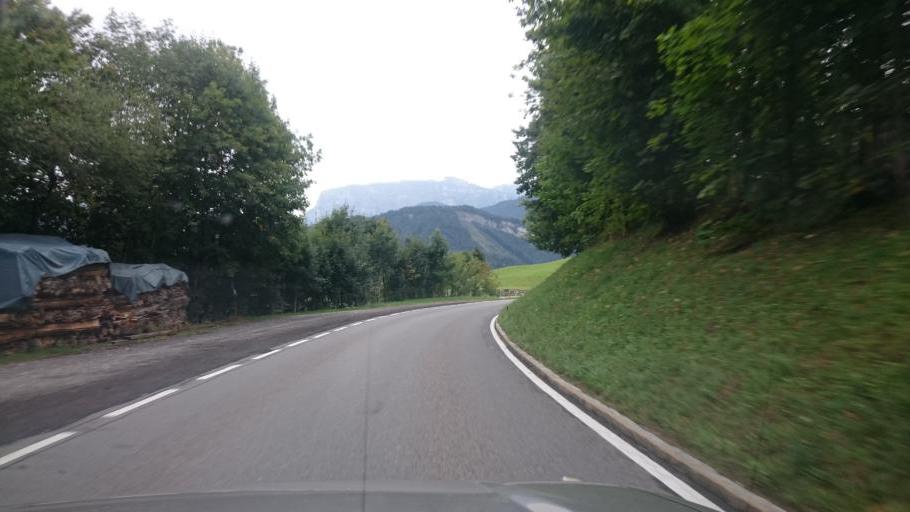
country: AT
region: Vorarlberg
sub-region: Politischer Bezirk Bregenz
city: Andelsbuch
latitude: 47.4159
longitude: 9.8436
